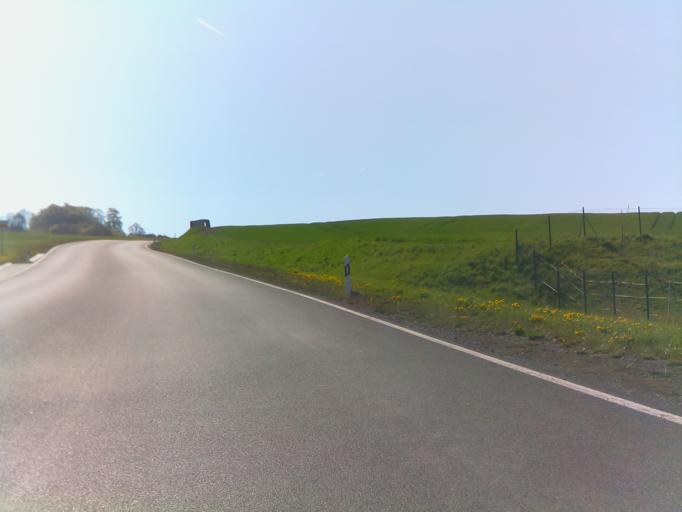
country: DE
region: Thuringia
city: Schleiz
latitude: 50.5681
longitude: 11.8130
